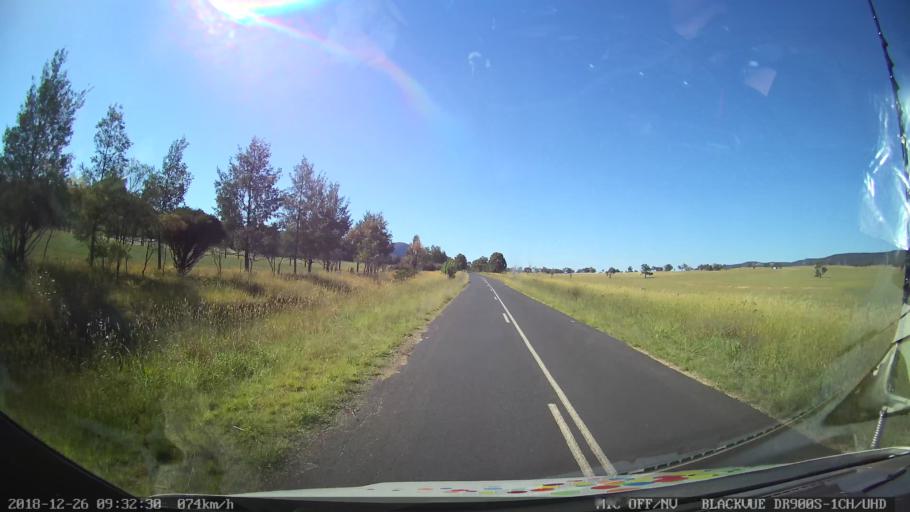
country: AU
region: New South Wales
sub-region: Mid-Western Regional
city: Kandos
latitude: -32.8851
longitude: 150.0325
